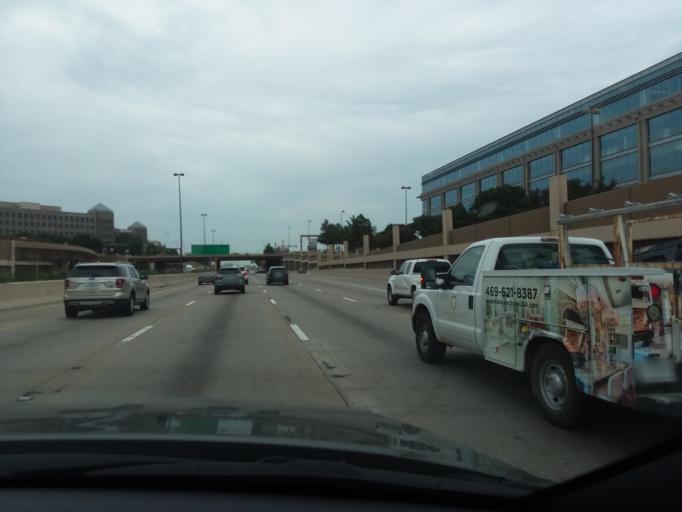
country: US
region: Texas
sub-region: Dallas County
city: University Park
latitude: 32.8694
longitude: -96.7701
